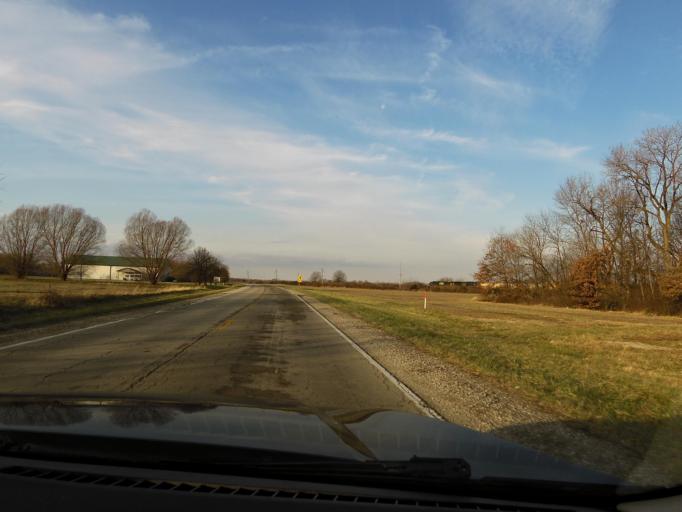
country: US
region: Illinois
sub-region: Bond County
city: Greenville
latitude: 38.9185
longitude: -89.2810
